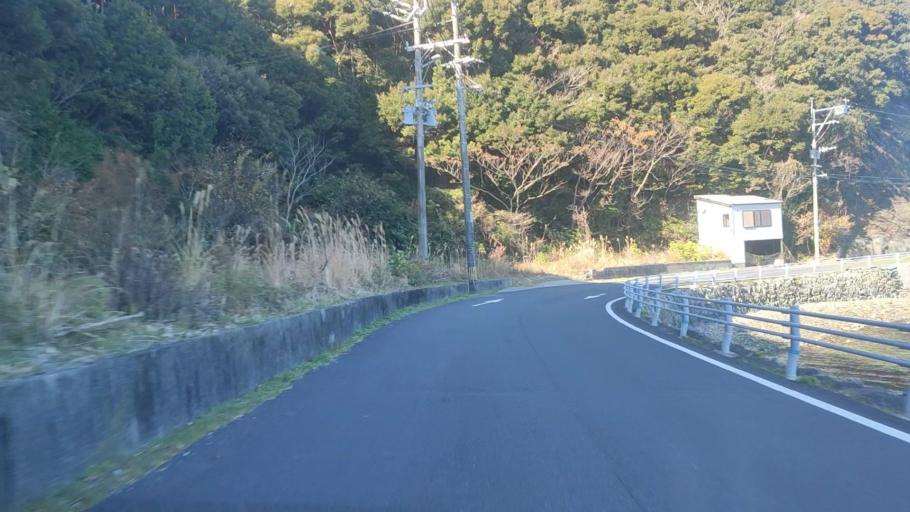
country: JP
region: Oita
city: Saiki
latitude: 32.8352
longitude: 131.9585
